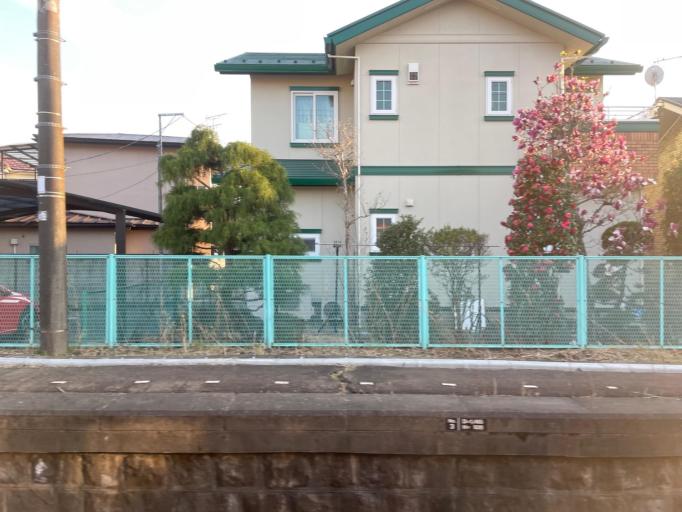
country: JP
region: Gunma
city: Takasaki
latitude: 36.3382
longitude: 139.0032
